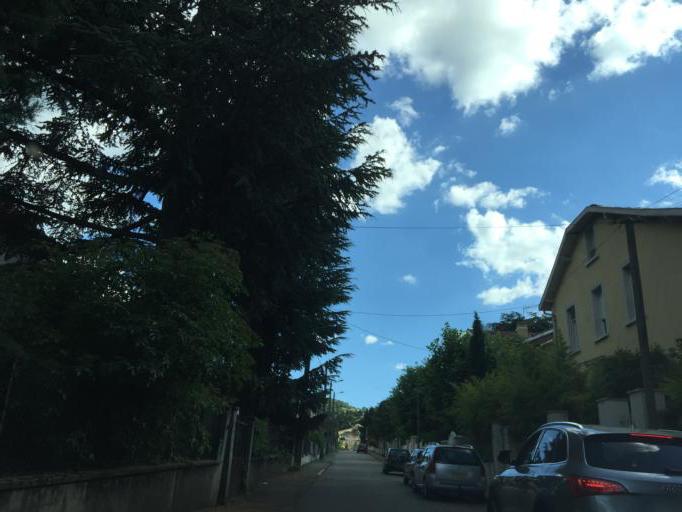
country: FR
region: Rhone-Alpes
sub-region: Departement de la Loire
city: Saint-Chamond
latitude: 45.4698
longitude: 4.5278
